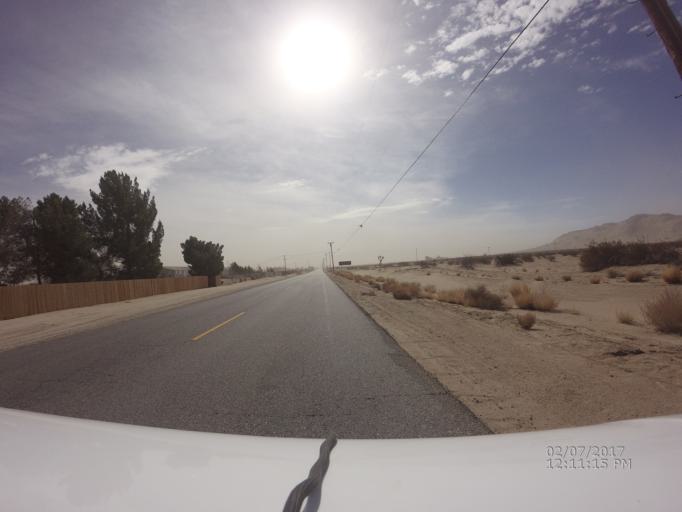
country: US
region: California
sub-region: Los Angeles County
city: Lake Los Angeles
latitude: 34.6696
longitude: -117.8275
